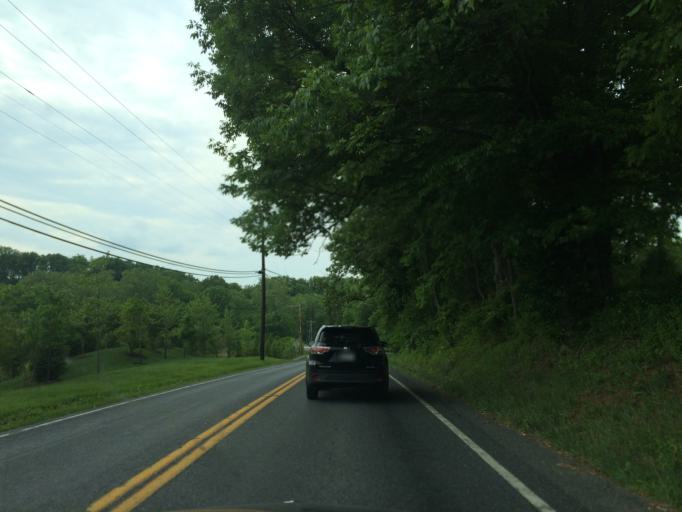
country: US
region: Maryland
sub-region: Howard County
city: Columbia
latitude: 39.2416
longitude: -76.9072
